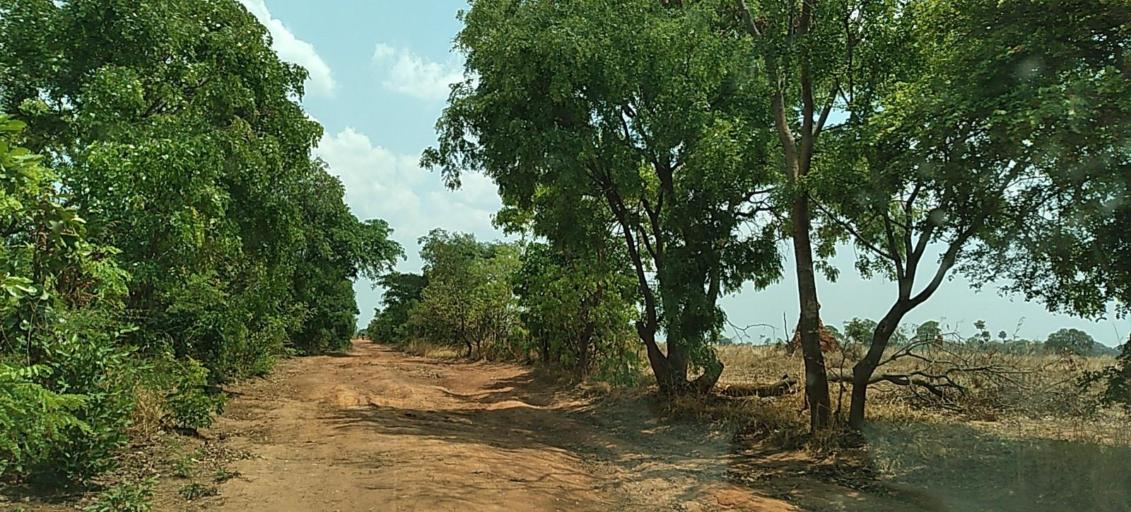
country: ZM
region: Copperbelt
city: Mpongwe
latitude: -13.6576
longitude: 28.0252
